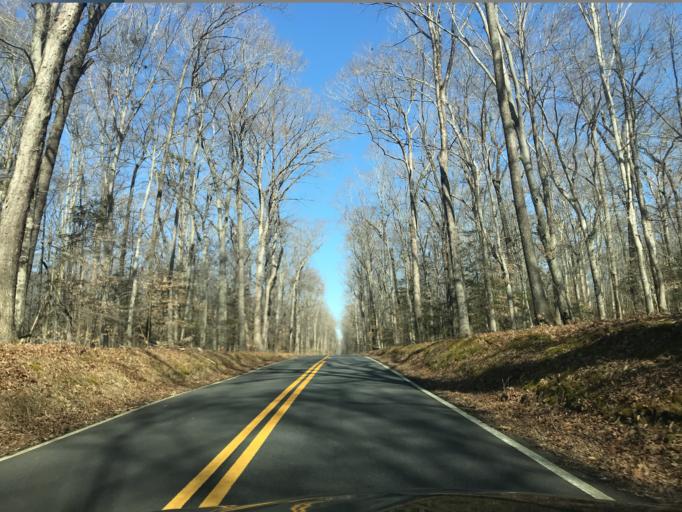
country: US
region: Virginia
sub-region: Prince William County
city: Cherry Hill
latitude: 38.5032
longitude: -77.2496
